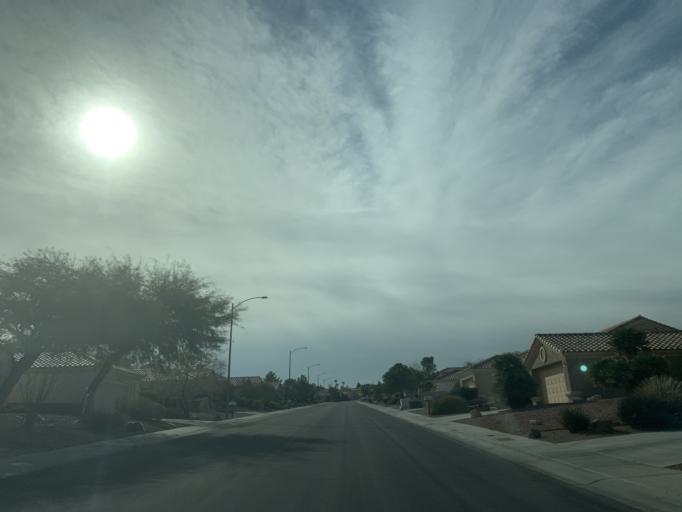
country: US
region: Nevada
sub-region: Clark County
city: Summerlin South
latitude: 36.2156
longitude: -115.3283
